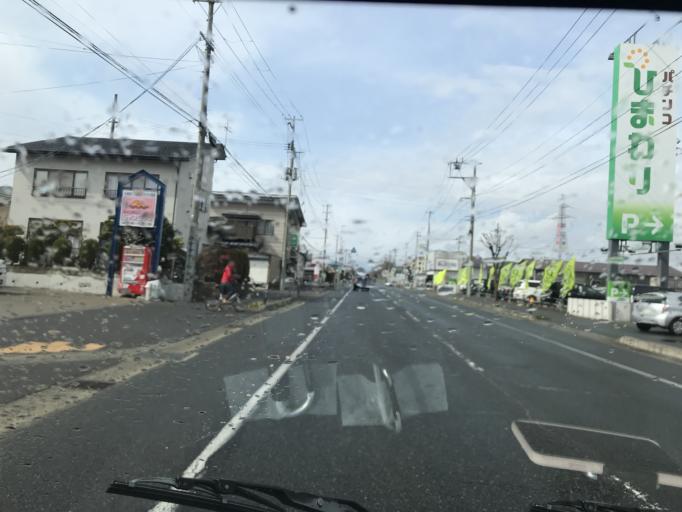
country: JP
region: Iwate
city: Kitakami
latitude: 39.3074
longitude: 141.1149
